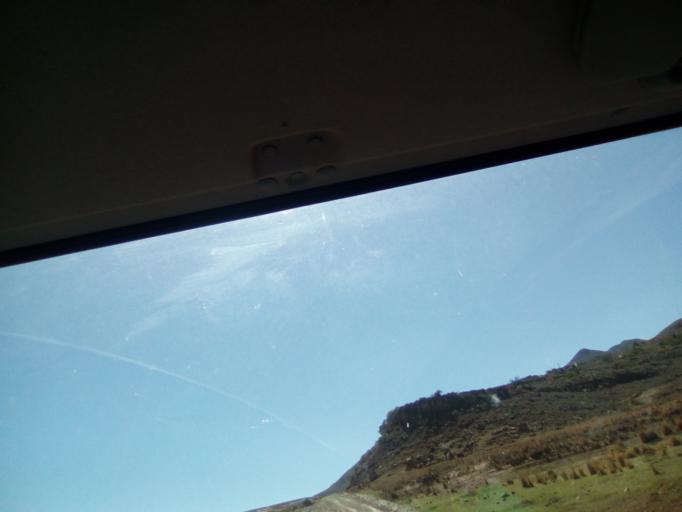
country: LS
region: Qacha's Nek
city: Qacha's Nek
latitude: -30.0438
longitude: 28.6490
